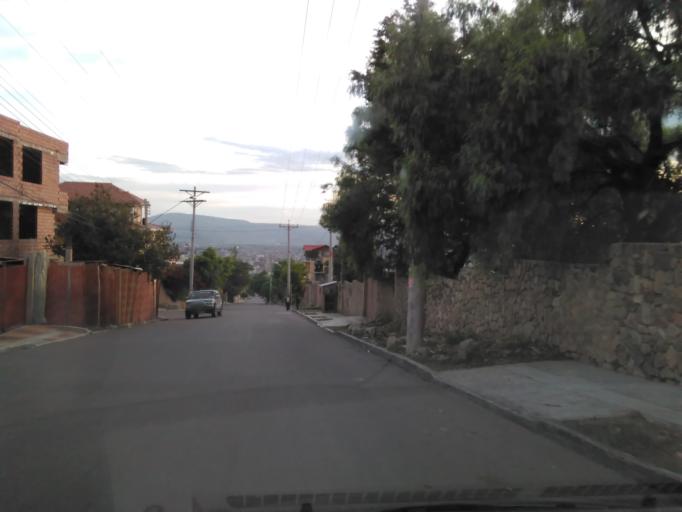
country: BO
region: Cochabamba
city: Cochabamba
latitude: -17.3562
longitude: -66.1600
